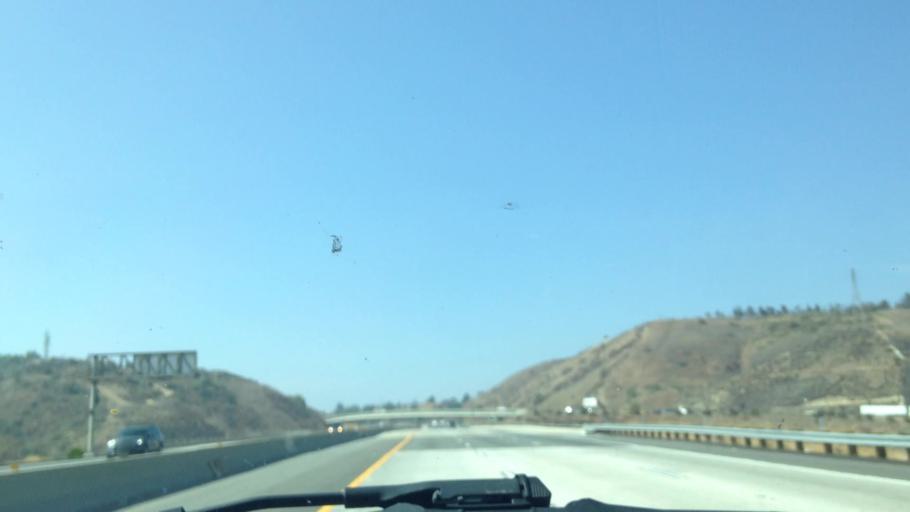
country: US
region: California
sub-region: Los Angeles County
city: Diamond Bar
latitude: 34.0637
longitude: -117.8060
